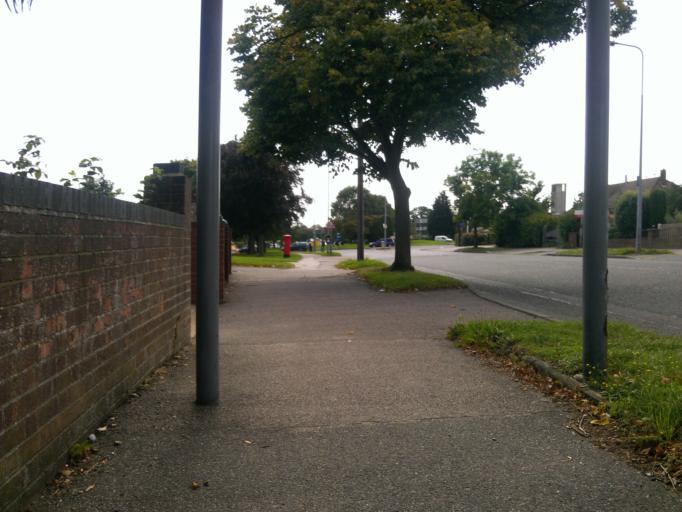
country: GB
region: England
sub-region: Essex
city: Clacton-on-Sea
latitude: 51.8058
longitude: 1.1487
